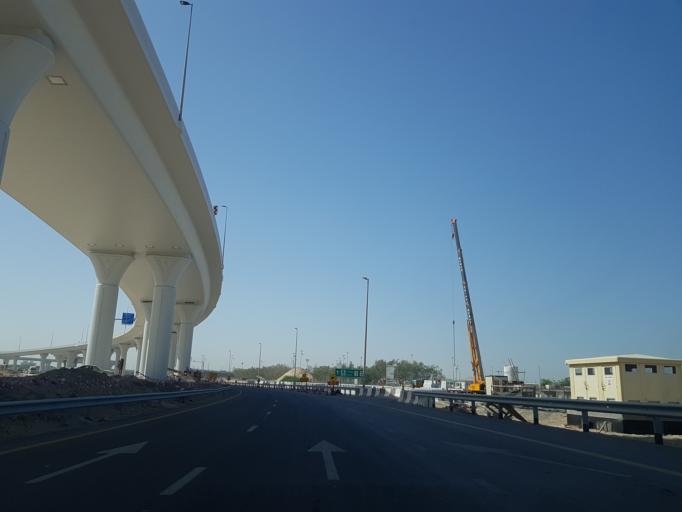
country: AE
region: Dubai
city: Dubai
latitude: 25.0196
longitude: 55.0958
